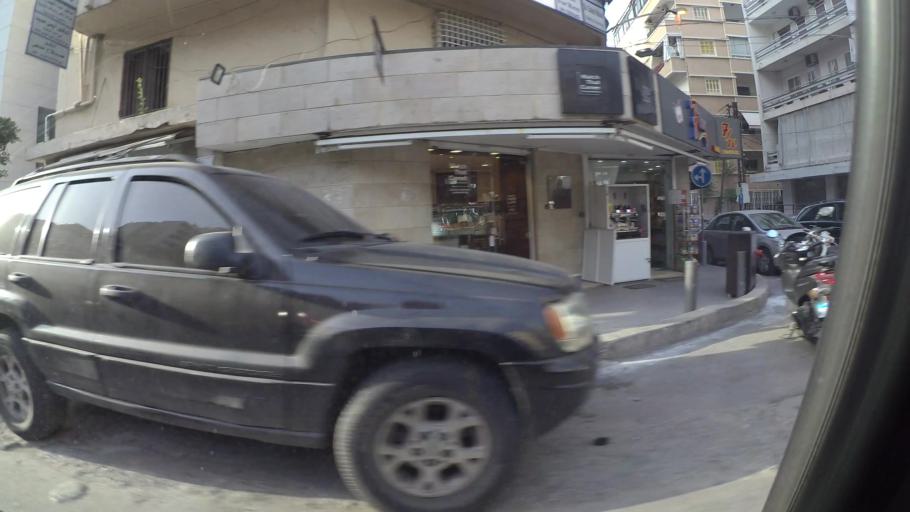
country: LB
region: Beyrouth
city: Ra's Bayrut
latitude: 33.8966
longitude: 35.4868
